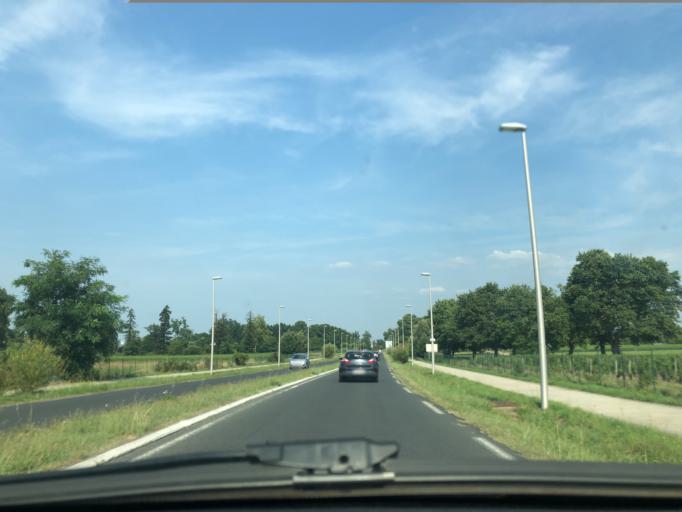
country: FR
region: Aquitaine
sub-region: Departement de la Gironde
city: Merignac
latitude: 44.8235
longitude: -0.6432
